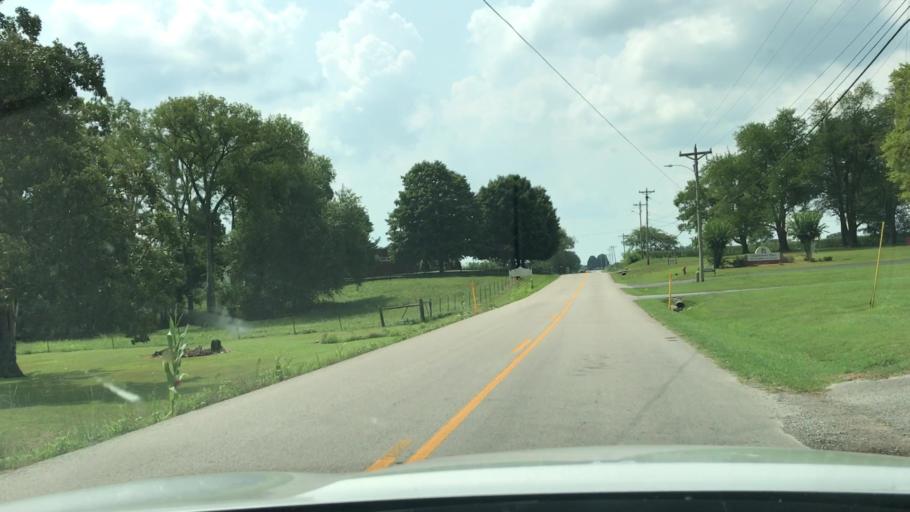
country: US
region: Kentucky
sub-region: Todd County
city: Elkton
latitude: 36.7993
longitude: -87.1487
